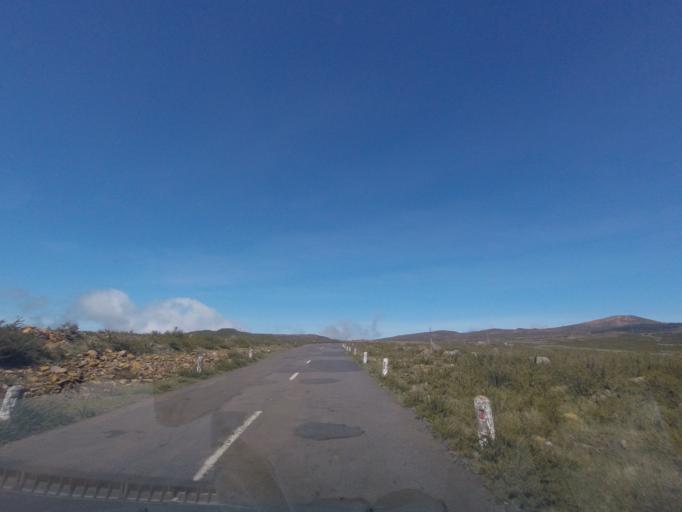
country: PT
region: Madeira
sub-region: Calheta
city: Arco da Calheta
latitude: 32.7524
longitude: -17.0989
